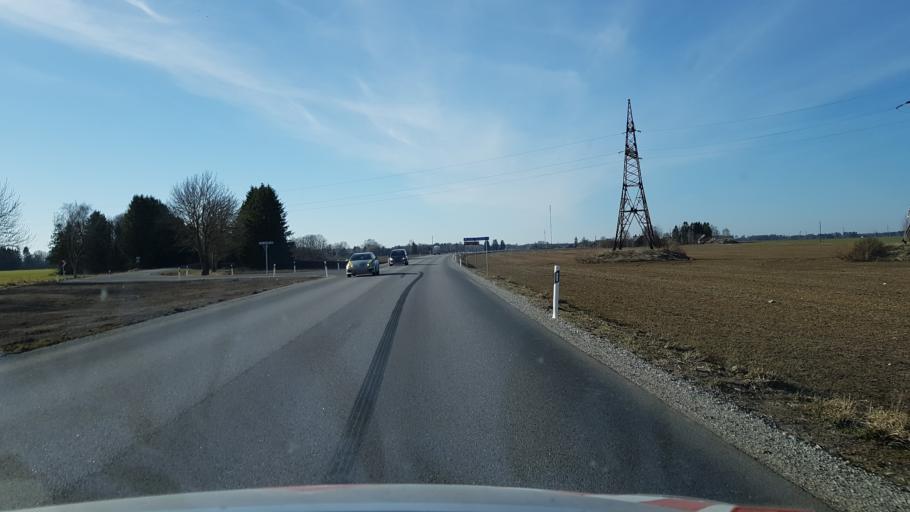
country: EE
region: Laeaene-Virumaa
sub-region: Vinni vald
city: Vinni
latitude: 59.2397
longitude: 26.4896
